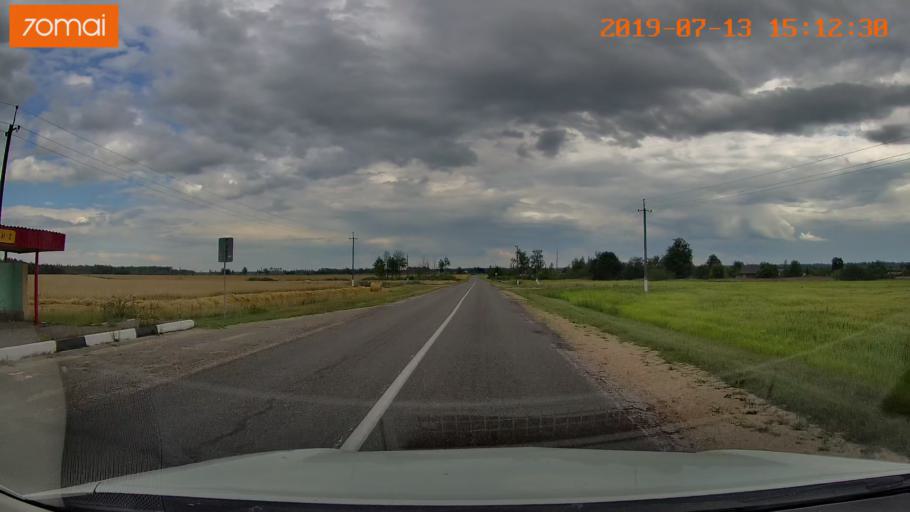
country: BY
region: Mogilev
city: Hlusha
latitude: 53.1480
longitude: 28.7927
